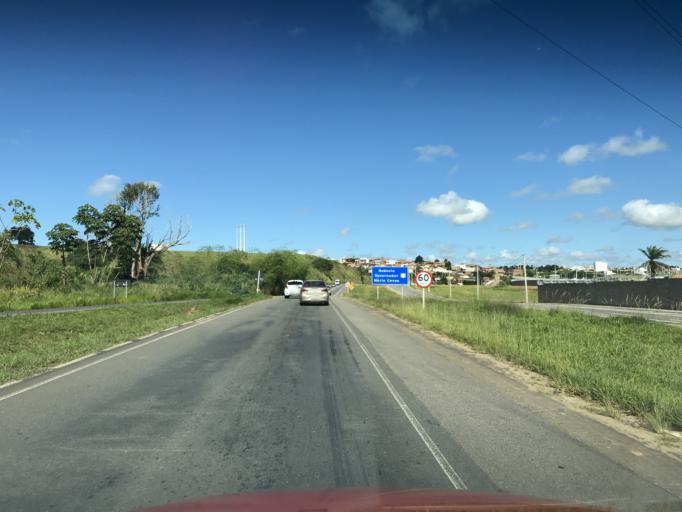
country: BR
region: Bahia
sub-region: Santo Antonio De Jesus
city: Santo Antonio de Jesus
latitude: -12.9527
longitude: -39.2554
